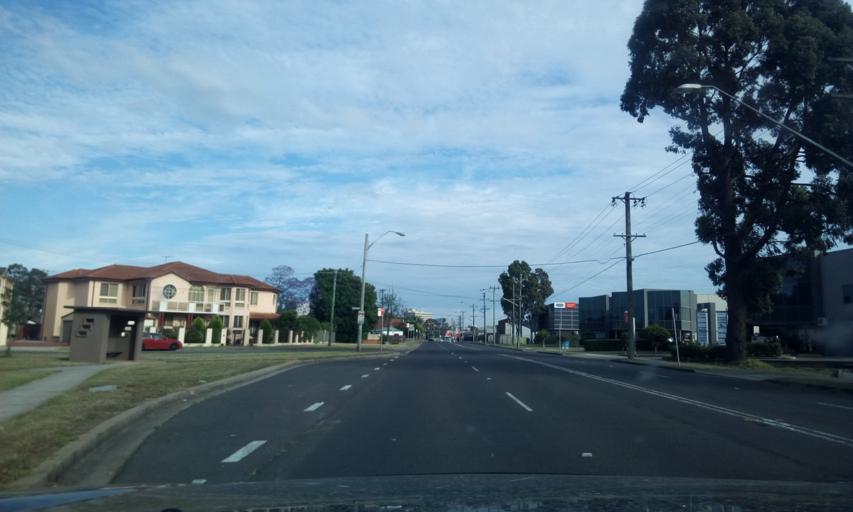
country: AU
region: New South Wales
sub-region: Fairfield
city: Liverpool
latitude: -33.9319
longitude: 150.9335
